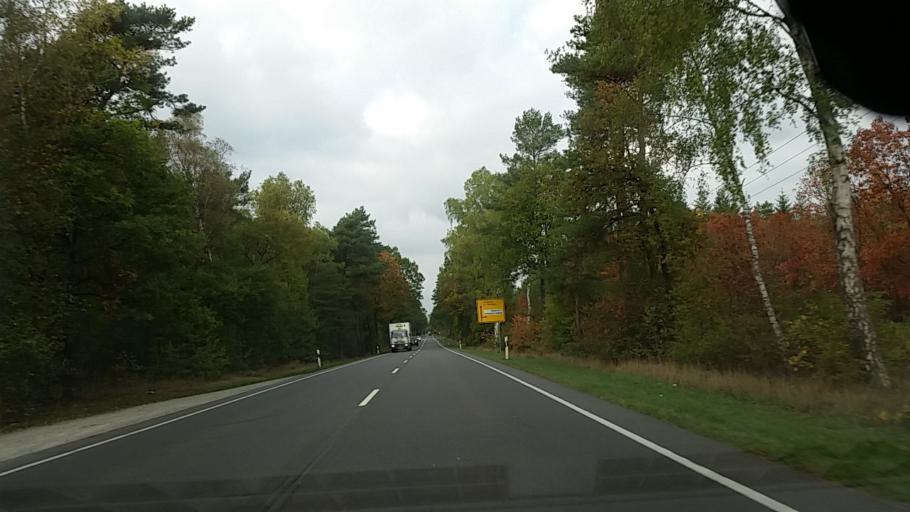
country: DE
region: Lower Saxony
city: Wesendorf
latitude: 52.5857
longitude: 10.4957
